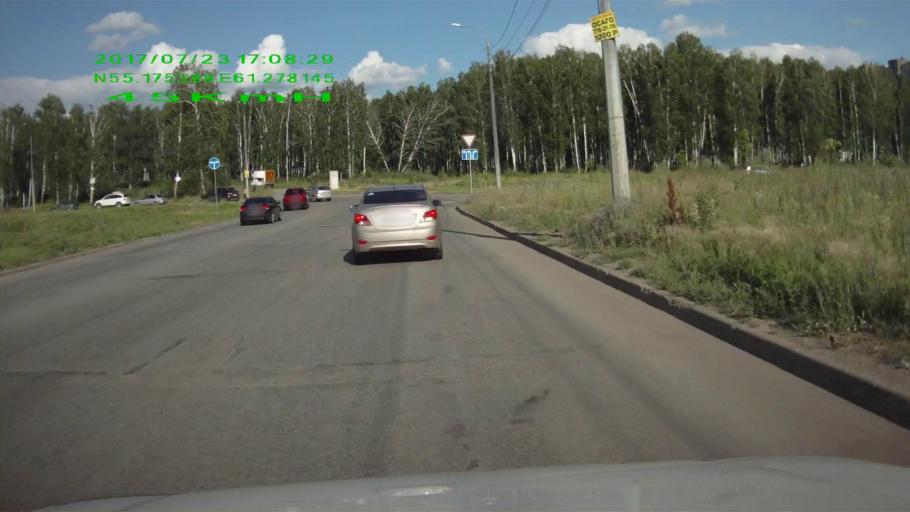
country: RU
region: Chelyabinsk
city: Roshchino
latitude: 55.1747
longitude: 61.2783
